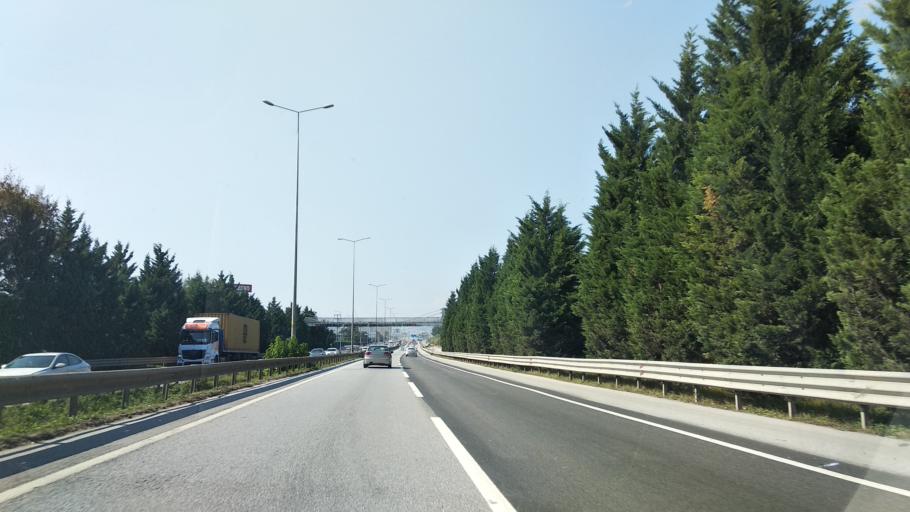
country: TR
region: Kocaeli
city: Kosekoy
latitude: 40.7561
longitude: 30.0054
